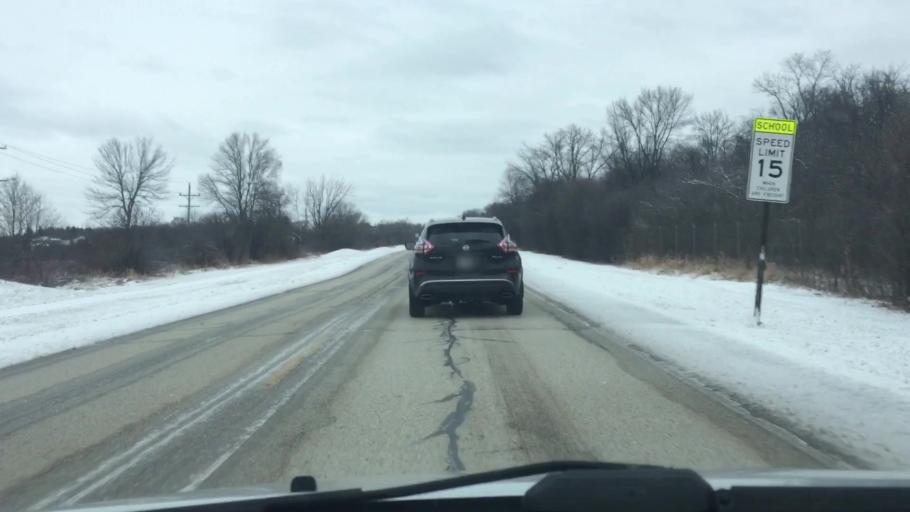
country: US
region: Wisconsin
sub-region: Waukesha County
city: Brookfield
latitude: 43.0468
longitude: -88.1060
